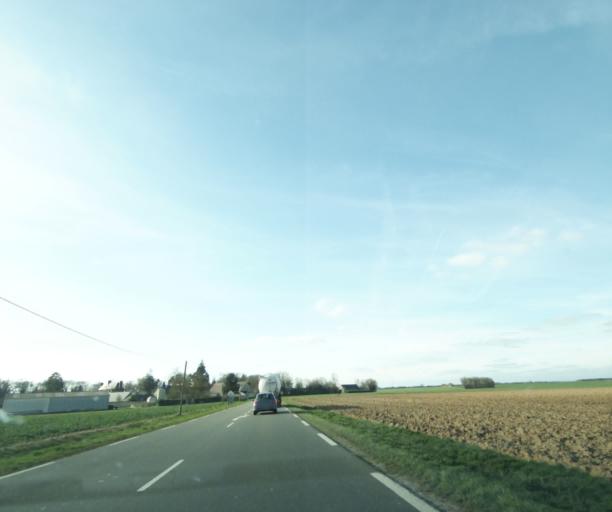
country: FR
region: Ile-de-France
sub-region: Departement des Yvelines
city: Ablis
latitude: 48.4681
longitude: 1.8708
